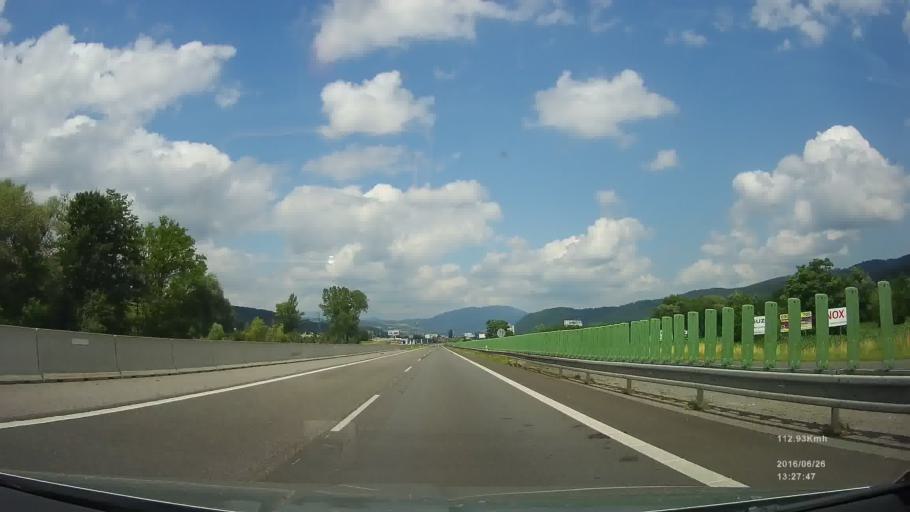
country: SK
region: Banskobystricky
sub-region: Okres Banska Bystrica
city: Banska Bystrica
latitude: 48.6891
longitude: 19.1320
